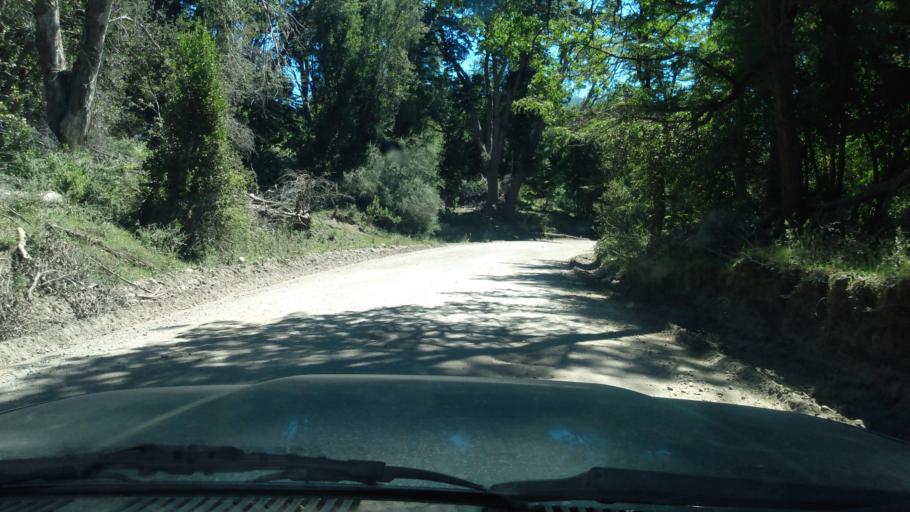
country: AR
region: Neuquen
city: Villa La Angostura
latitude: -40.6205
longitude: -71.5772
